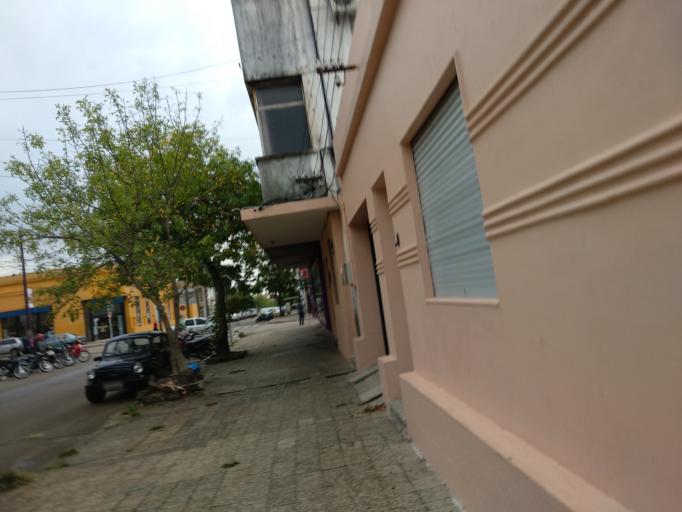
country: UY
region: Artigas
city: Artigas
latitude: -30.4020
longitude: -56.4662
